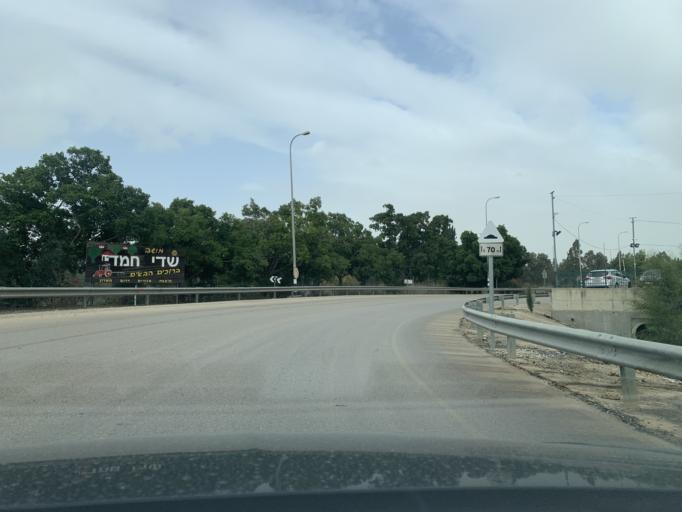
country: IL
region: Central District
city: Jaljulya
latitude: 32.1547
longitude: 34.9468
